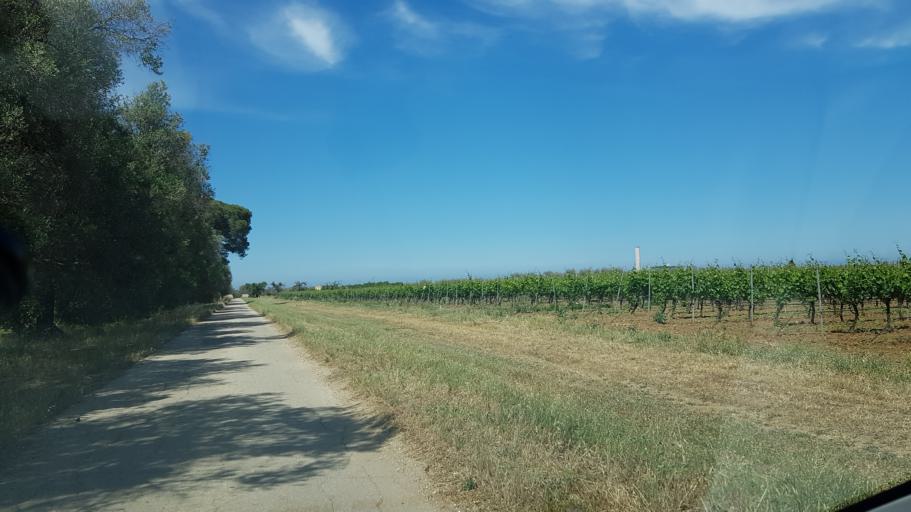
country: IT
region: Apulia
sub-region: Provincia di Brindisi
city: San Pietro Vernotico
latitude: 40.5375
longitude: 17.9968
